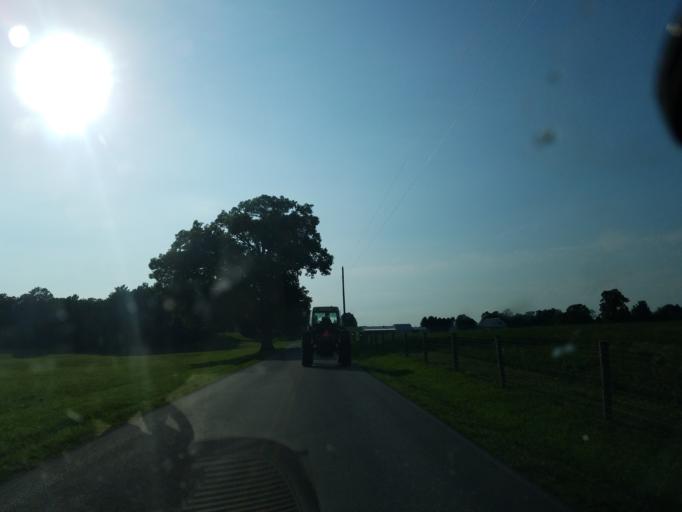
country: US
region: Ohio
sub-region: Adams County
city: West Union
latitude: 38.8854
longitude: -83.5052
